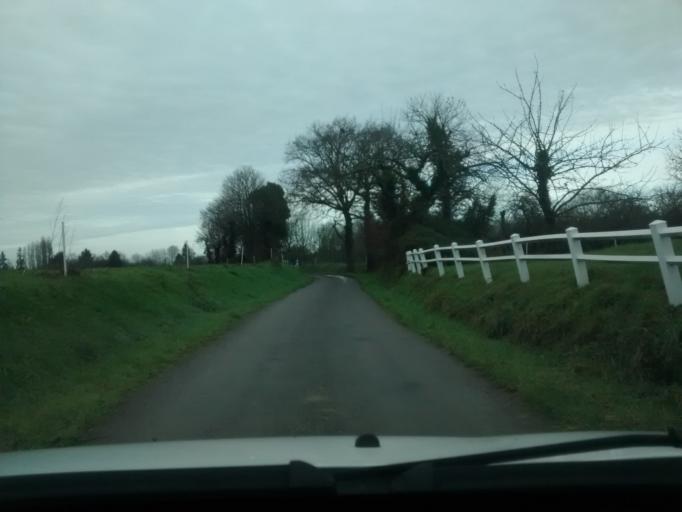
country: FR
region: Brittany
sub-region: Departement d'Ille-et-Vilaine
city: Montgermont
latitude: 48.1372
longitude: -1.7087
